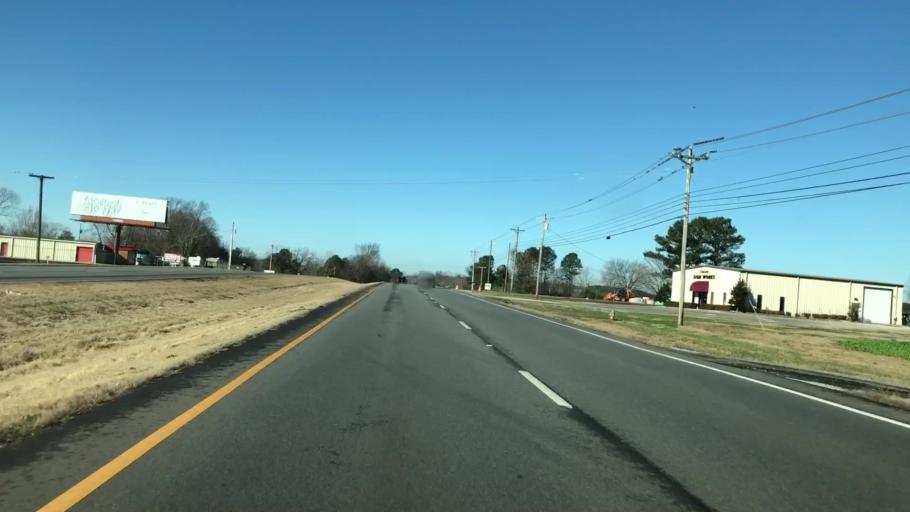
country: US
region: Alabama
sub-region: Limestone County
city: Athens
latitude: 34.7706
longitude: -86.9049
